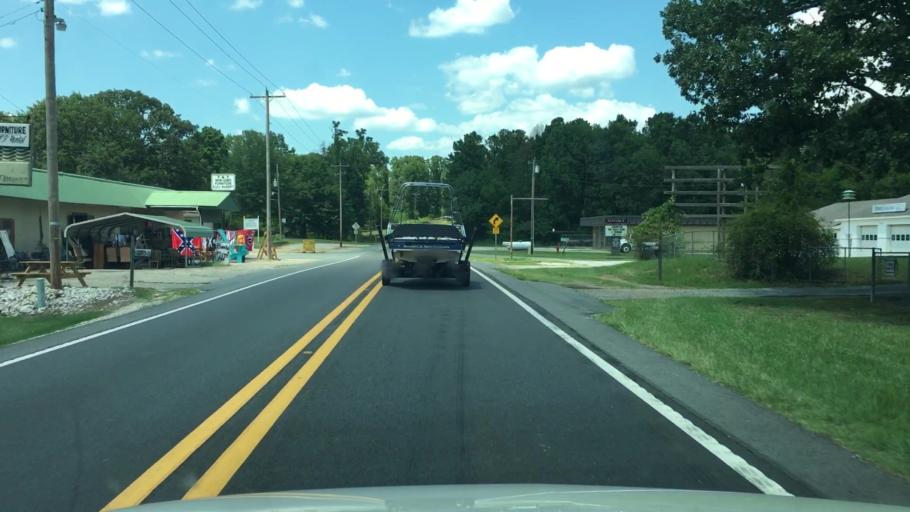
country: US
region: Arkansas
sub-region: Garland County
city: Lake Hamilton
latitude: 34.2835
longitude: -93.1631
